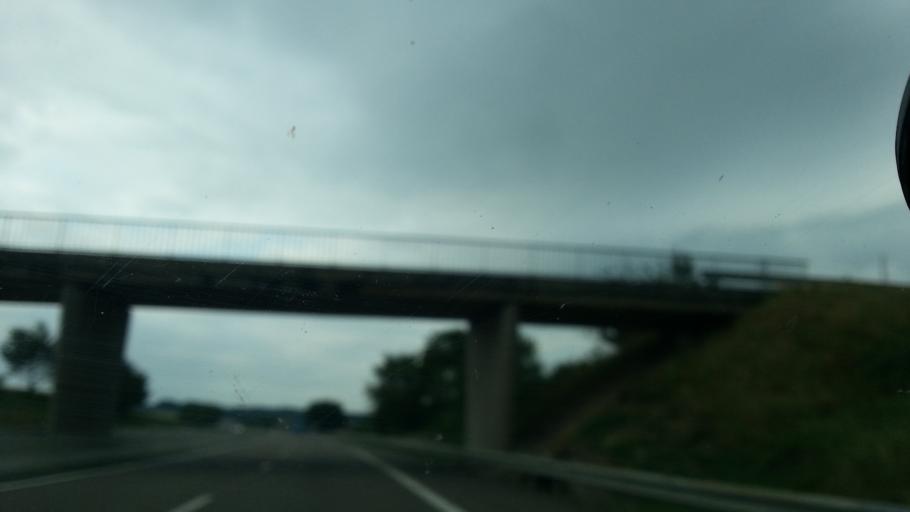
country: FR
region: Franche-Comte
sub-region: Departement du Doubs
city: Saint-Vit
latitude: 47.2102
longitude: 5.8363
